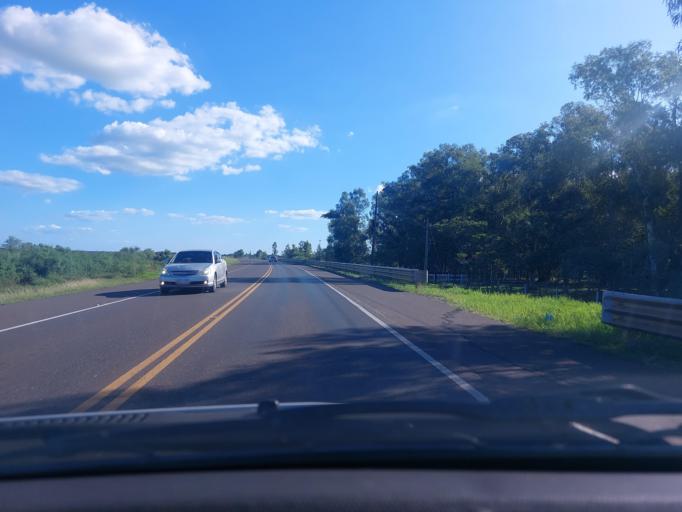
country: PY
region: Cordillera
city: Arroyos y Esteros
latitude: -24.8951
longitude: -56.9549
